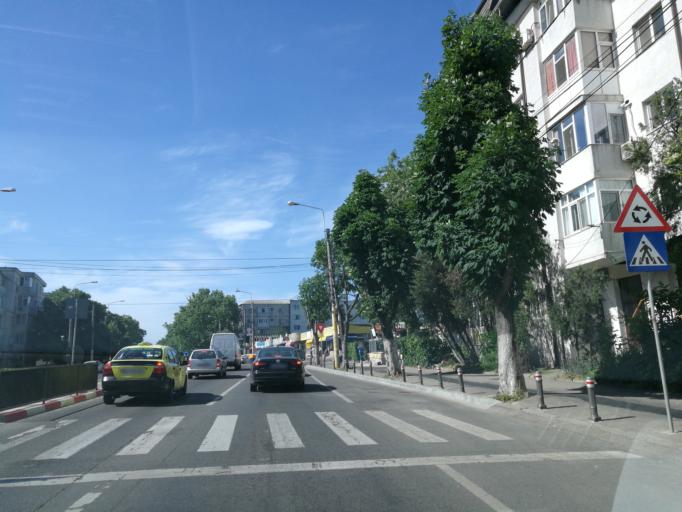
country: RO
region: Constanta
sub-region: Municipiul Constanta
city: Constanta
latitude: 44.1971
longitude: 28.6239
